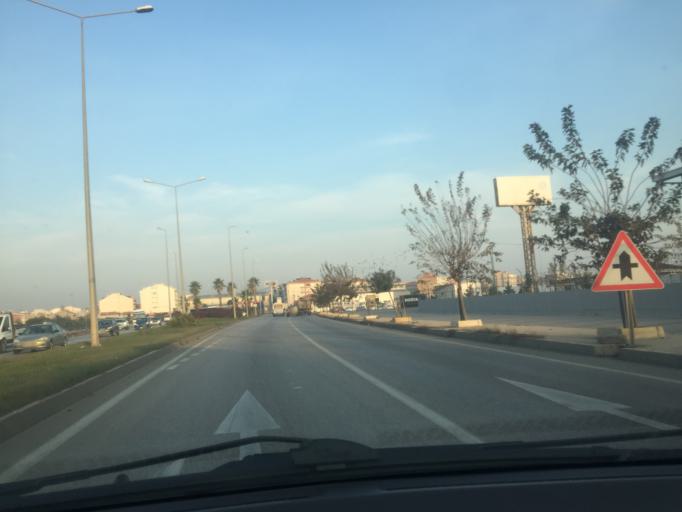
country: TR
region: Balikesir
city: Bandirma
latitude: 40.3330
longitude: 27.9940
